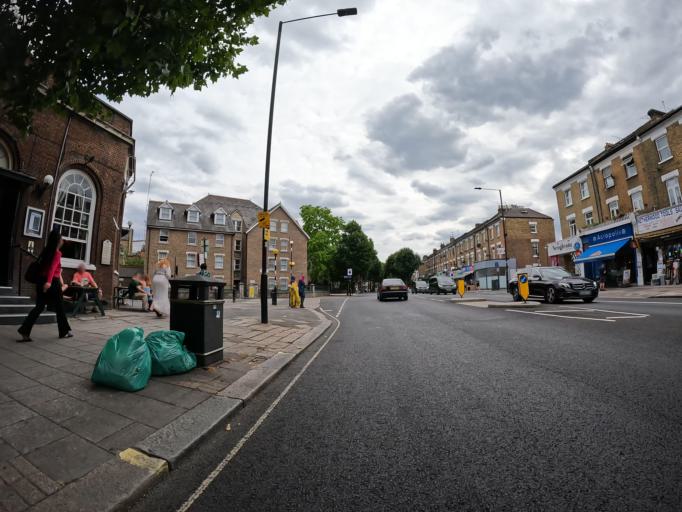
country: GB
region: England
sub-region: Greater London
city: Hammersmith
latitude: 51.5003
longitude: -0.2218
